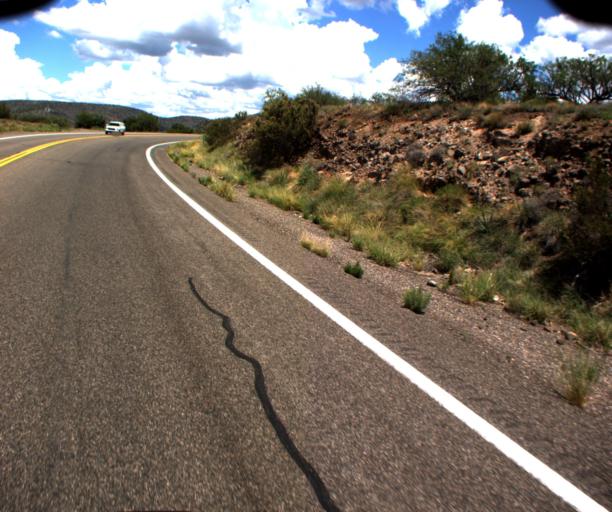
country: US
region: Arizona
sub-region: Yavapai County
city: Lake Montezuma
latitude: 34.4882
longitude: -111.6966
